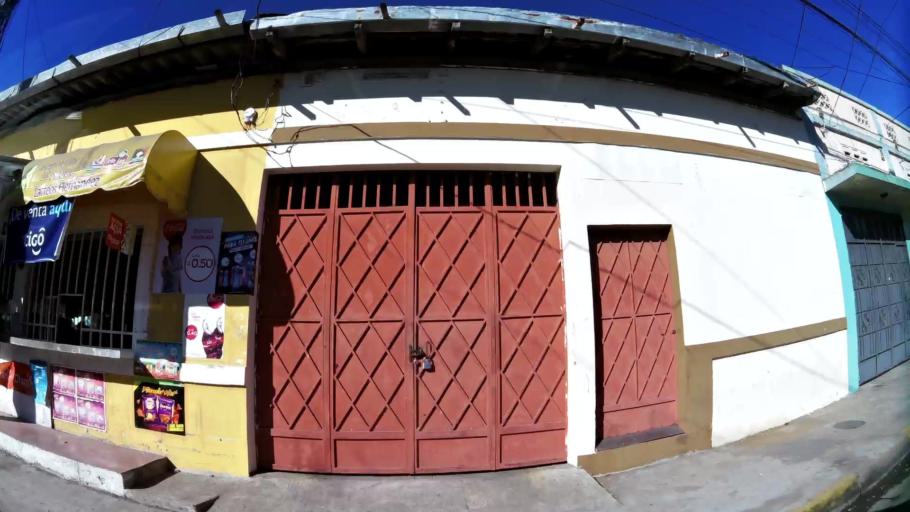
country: SV
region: San Miguel
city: San Miguel
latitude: 13.4748
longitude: -88.1774
